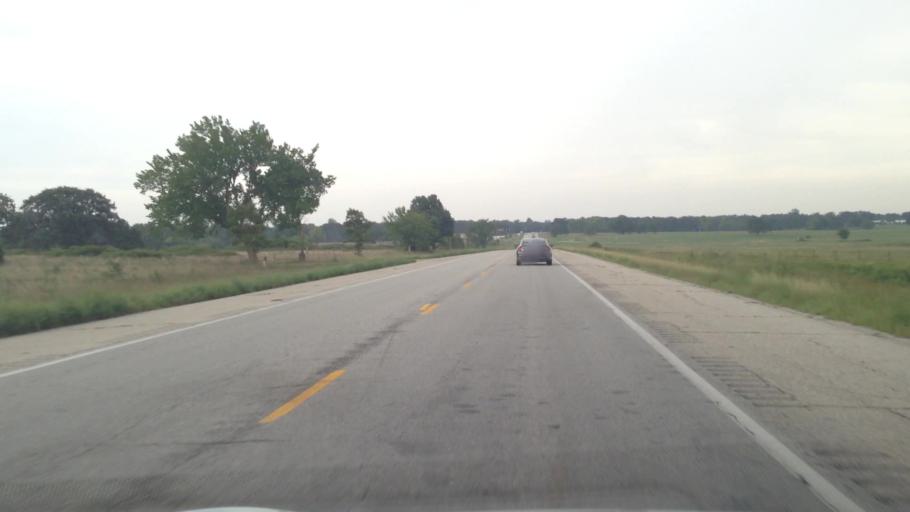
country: US
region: Kansas
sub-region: Cherokee County
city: Galena
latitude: 37.0132
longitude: -94.6297
